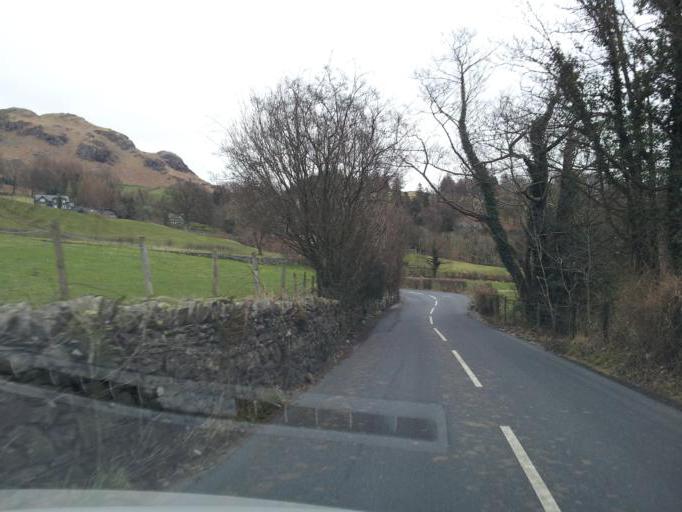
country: GB
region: England
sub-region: Cumbria
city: Ambleside
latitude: 54.4238
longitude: -3.0085
